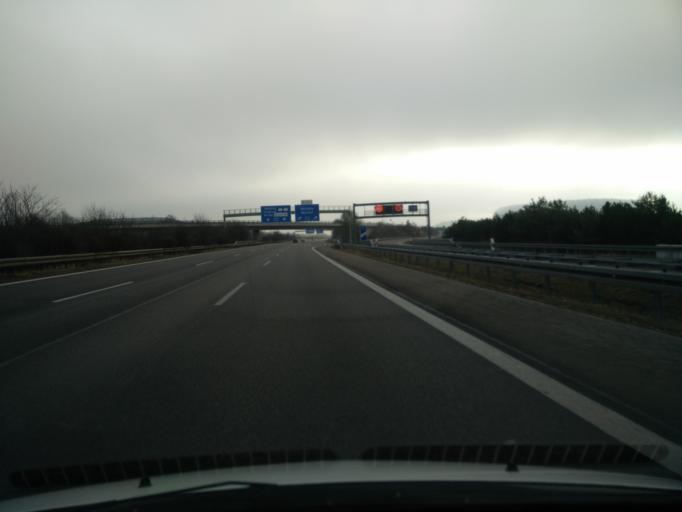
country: DE
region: Bavaria
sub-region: Upper Bavaria
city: Garching bei Munchen
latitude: 48.2260
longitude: 11.6152
